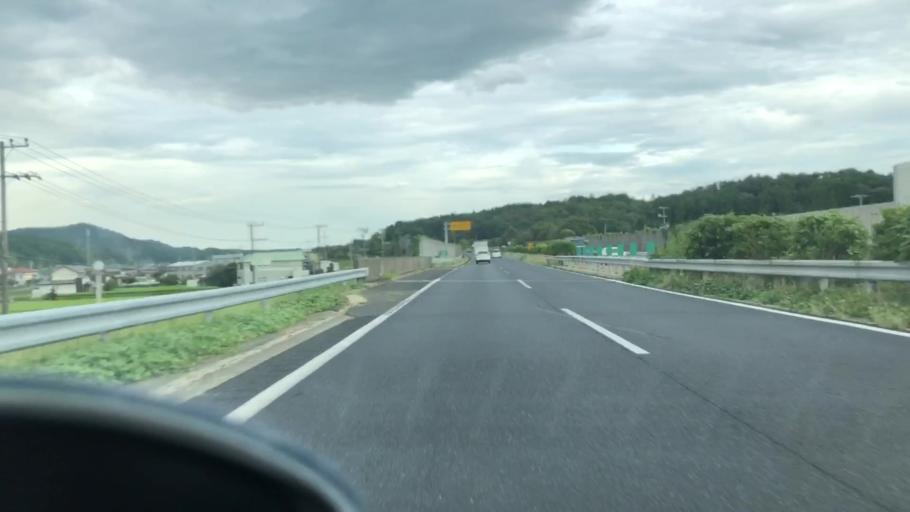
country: JP
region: Hyogo
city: Yashiro
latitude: 34.9193
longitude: 135.0084
